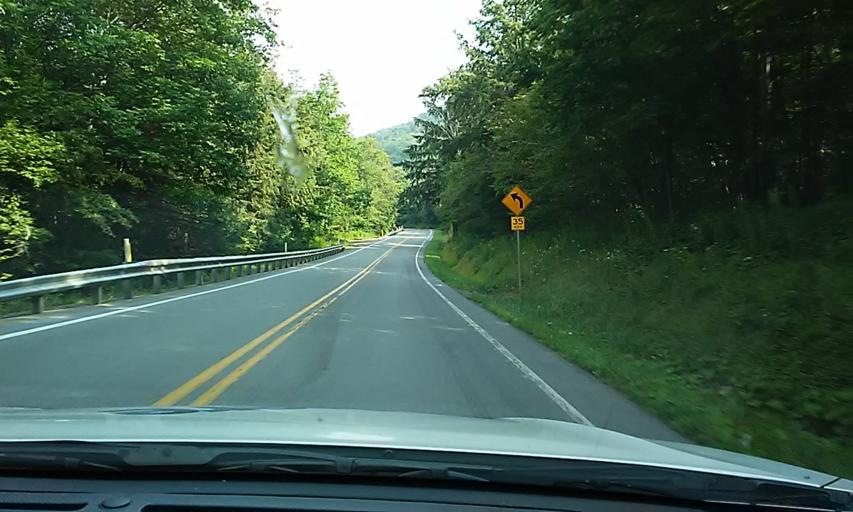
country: US
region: Pennsylvania
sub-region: Potter County
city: Galeton
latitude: 41.8162
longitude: -77.7921
